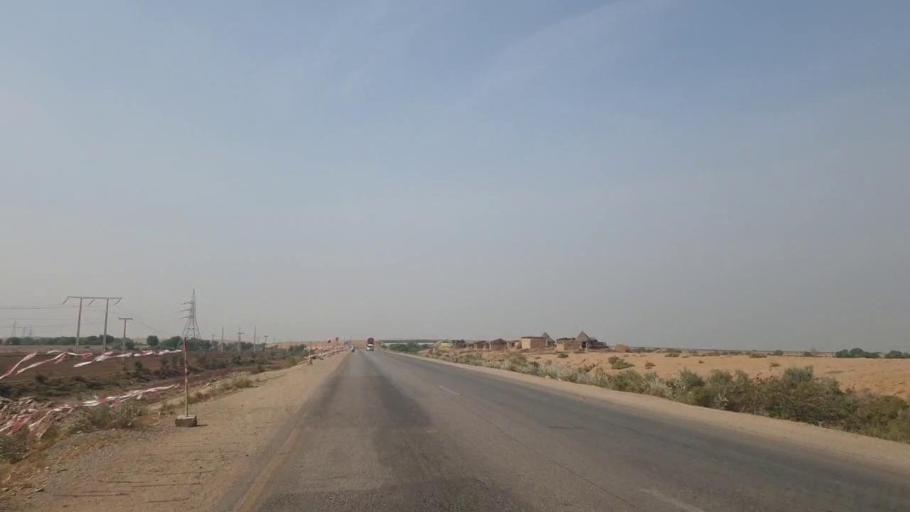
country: PK
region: Sindh
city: Sann
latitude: 26.1512
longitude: 68.0277
